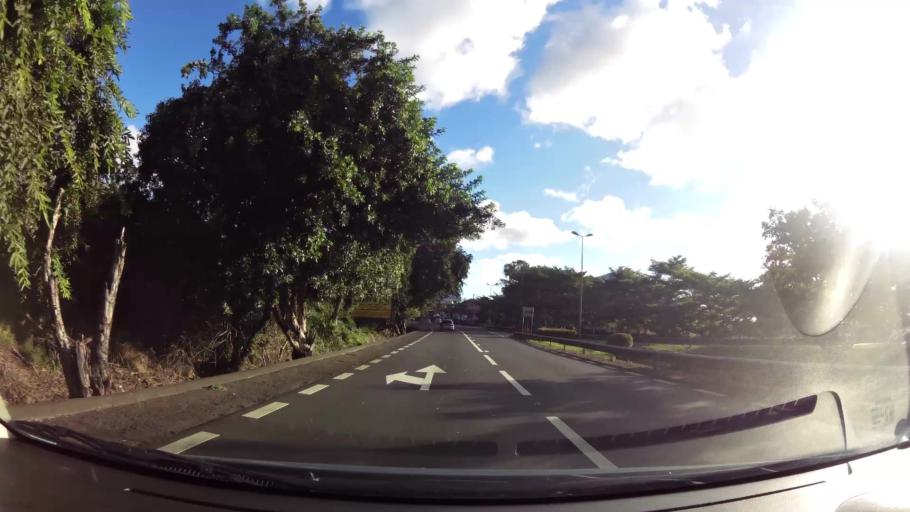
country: MU
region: Plaines Wilhems
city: Quatre Bornes
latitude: -20.2582
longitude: 57.4862
